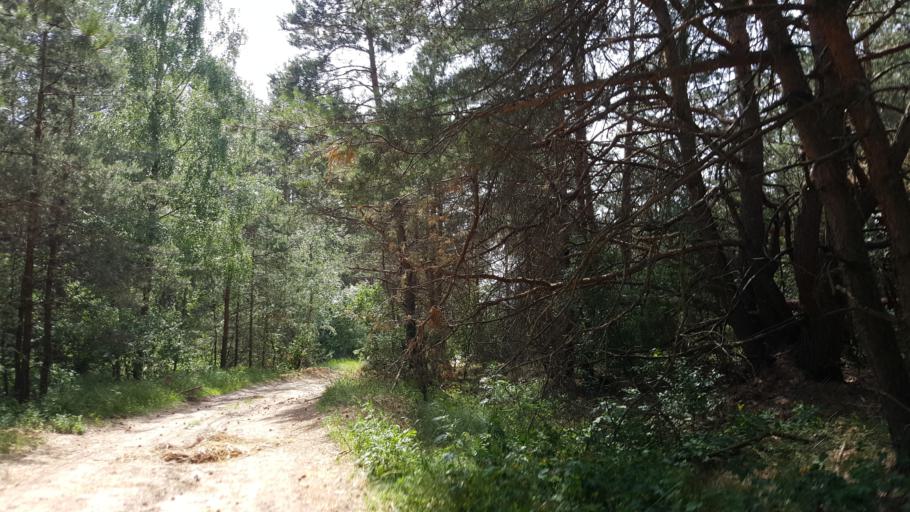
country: BY
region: Brest
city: Kamyanyets
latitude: 52.4702
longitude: 23.8308
